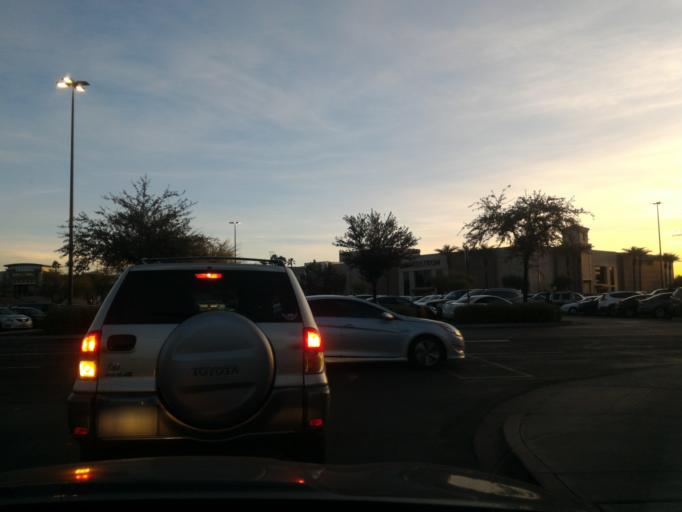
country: US
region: Arizona
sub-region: Maricopa County
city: Chandler
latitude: 33.3043
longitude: -111.8997
